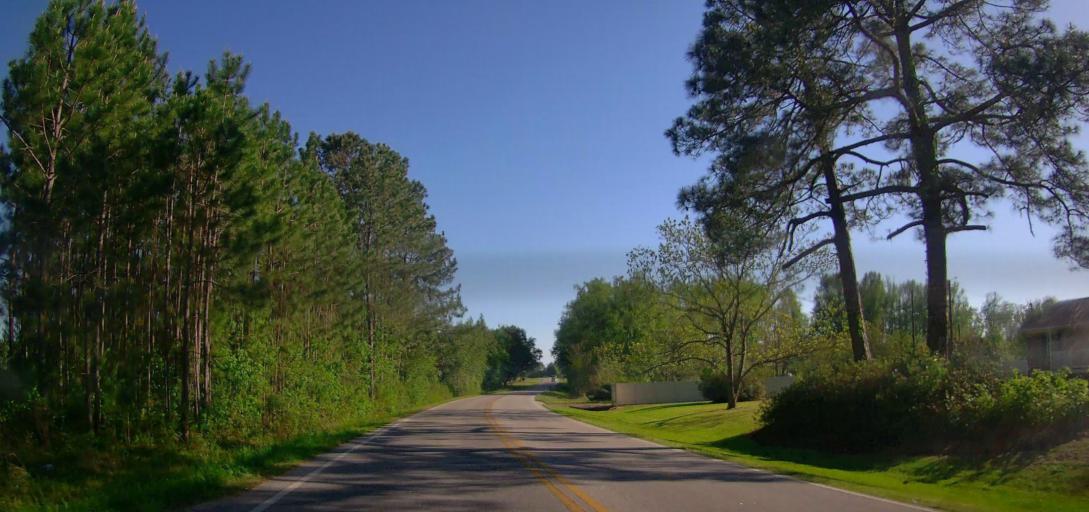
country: US
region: Georgia
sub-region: Ben Hill County
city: Fitzgerald
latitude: 31.7392
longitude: -83.2347
